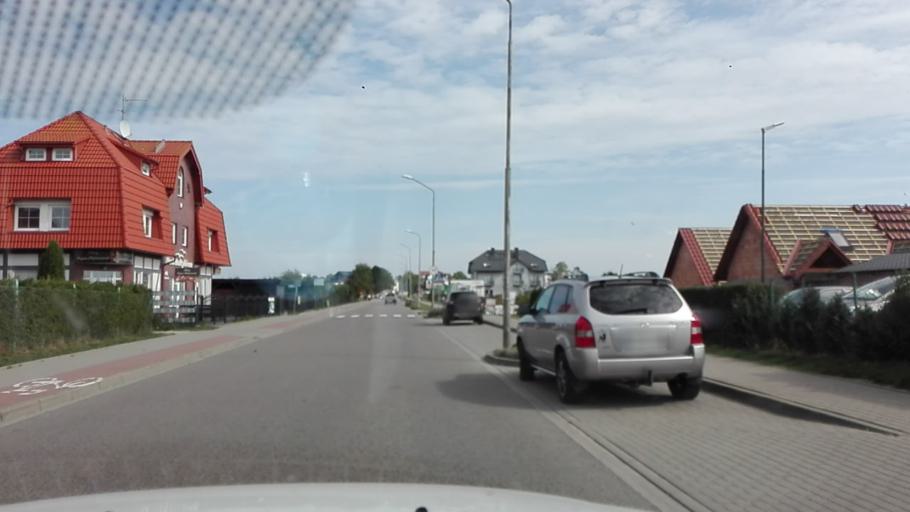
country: PL
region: West Pomeranian Voivodeship
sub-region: Powiat slawienski
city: Darlowo
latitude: 54.5389
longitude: 16.5341
